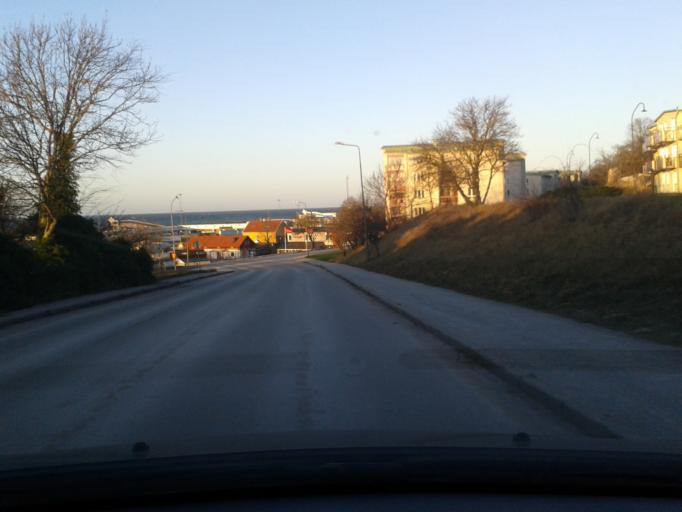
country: SE
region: Gotland
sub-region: Gotland
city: Visby
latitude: 57.6300
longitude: 18.2802
